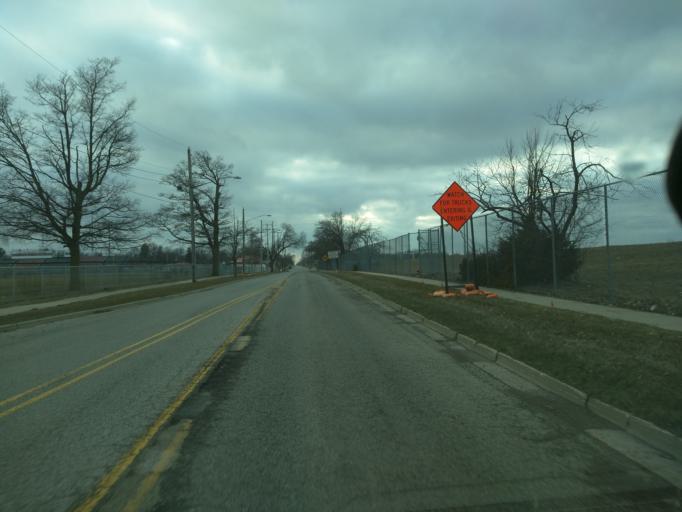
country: US
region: Michigan
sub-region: Ingham County
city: Edgemont Park
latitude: 42.7338
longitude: -84.5780
